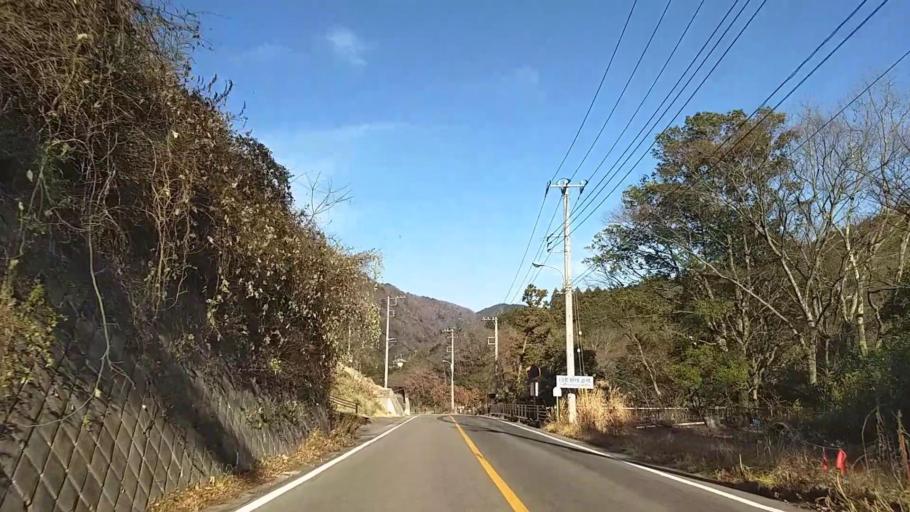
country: JP
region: Yamanashi
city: Uenohara
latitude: 35.5375
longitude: 139.1122
